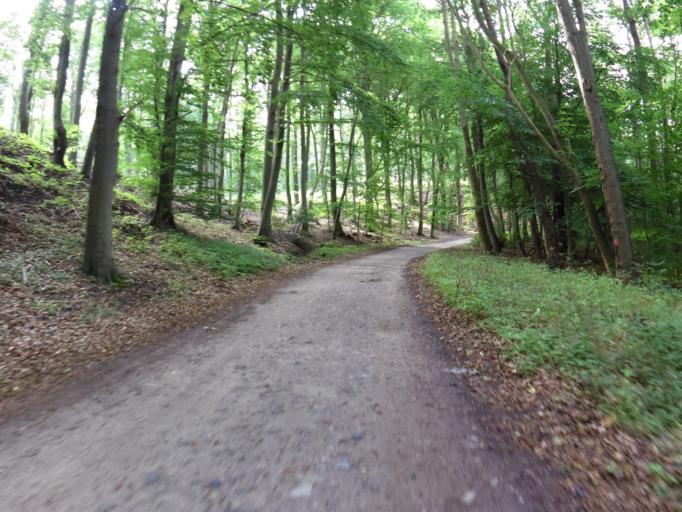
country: DE
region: Mecklenburg-Vorpommern
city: Seebad Bansin
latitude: 53.9709
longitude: 14.1073
